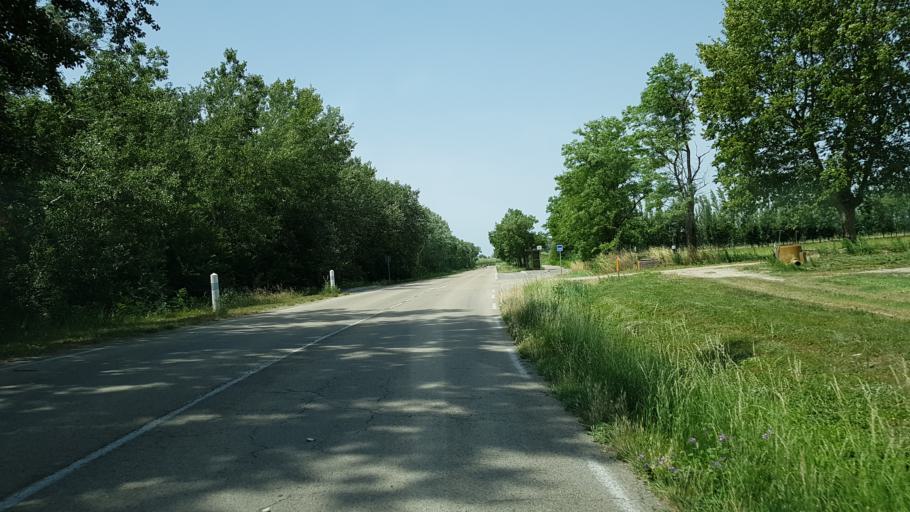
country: FR
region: Provence-Alpes-Cote d'Azur
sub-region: Departement des Bouches-du-Rhone
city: Saint-Martin-de-Crau
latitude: 43.5305
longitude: 4.7349
